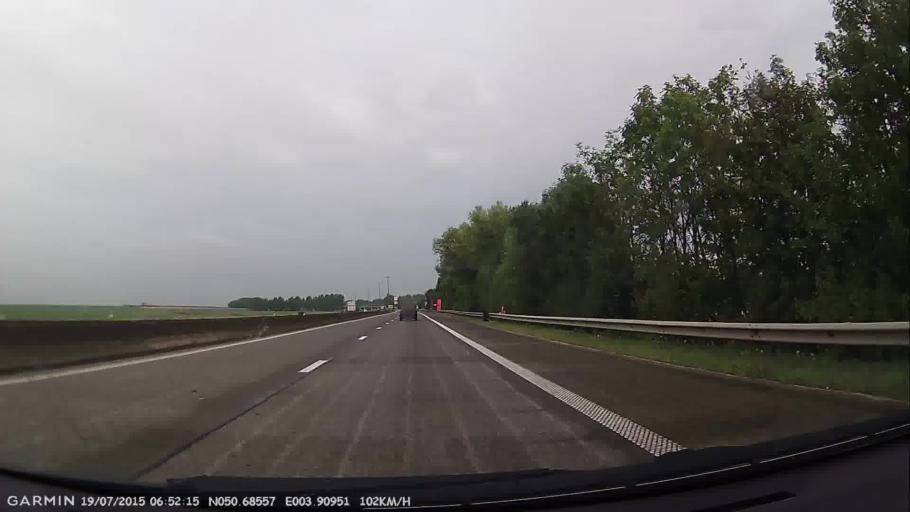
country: BE
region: Wallonia
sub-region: Province du Hainaut
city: Silly
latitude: 50.6856
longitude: 3.9094
